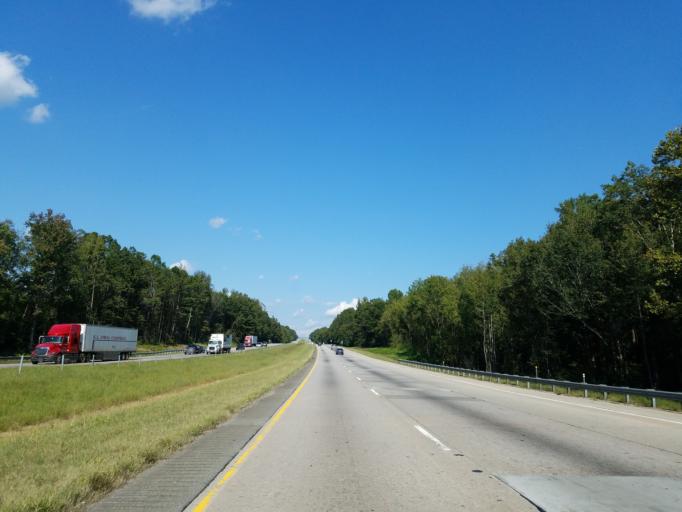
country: US
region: Georgia
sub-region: Banks County
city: Homer
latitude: 34.3009
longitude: -83.4003
